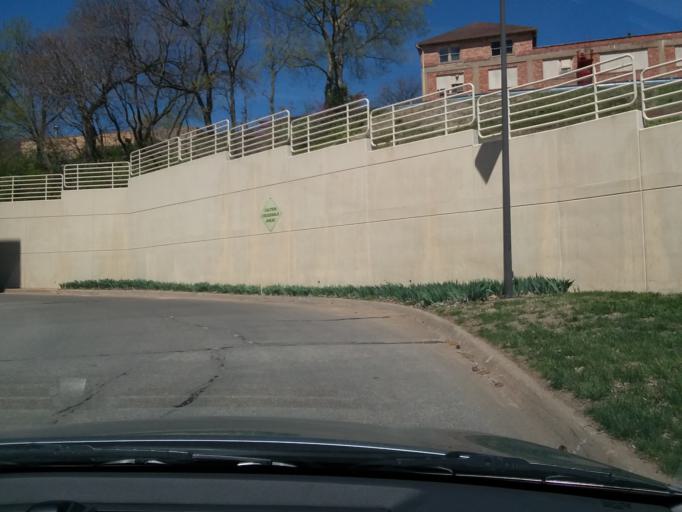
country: US
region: Kansas
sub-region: Douglas County
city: Lawrence
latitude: 38.9557
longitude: -95.2461
